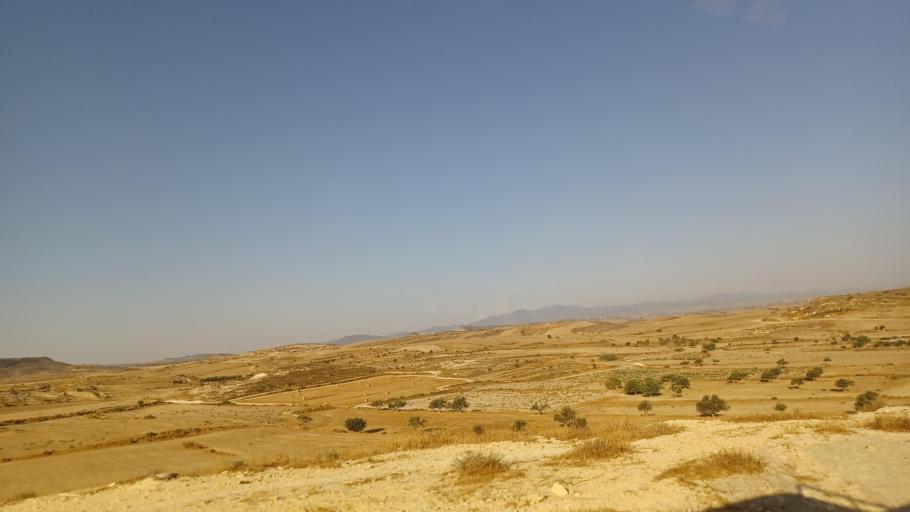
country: CY
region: Larnaka
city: Athienou
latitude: 35.0434
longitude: 33.5230
